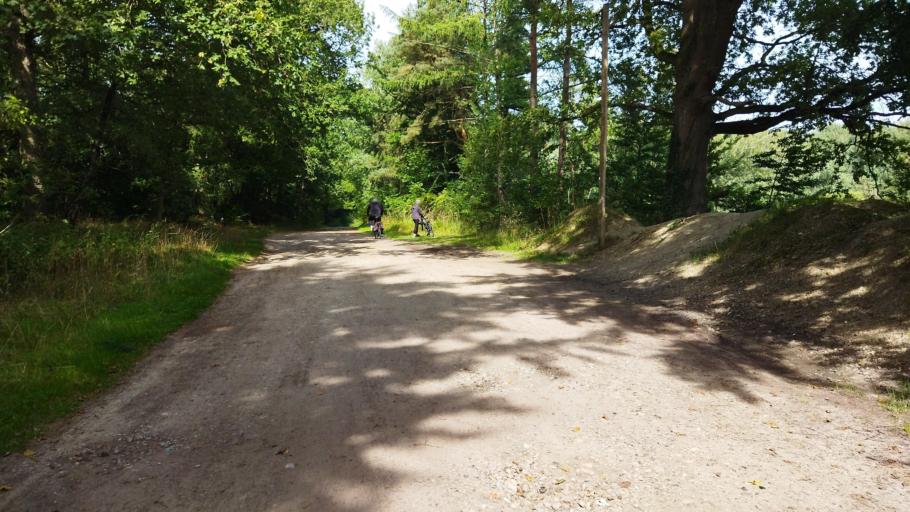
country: DE
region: Lower Saxony
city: Glandorf
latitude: 52.0996
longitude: 8.0363
